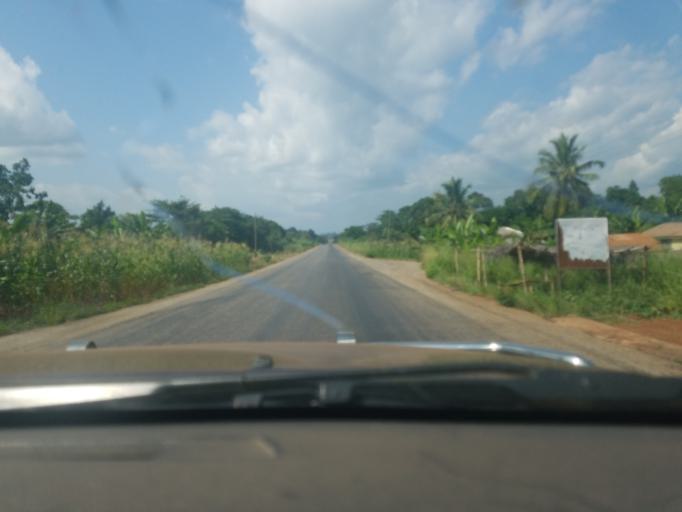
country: GH
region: Western
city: Bibiani
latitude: 6.8770
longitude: -2.4284
